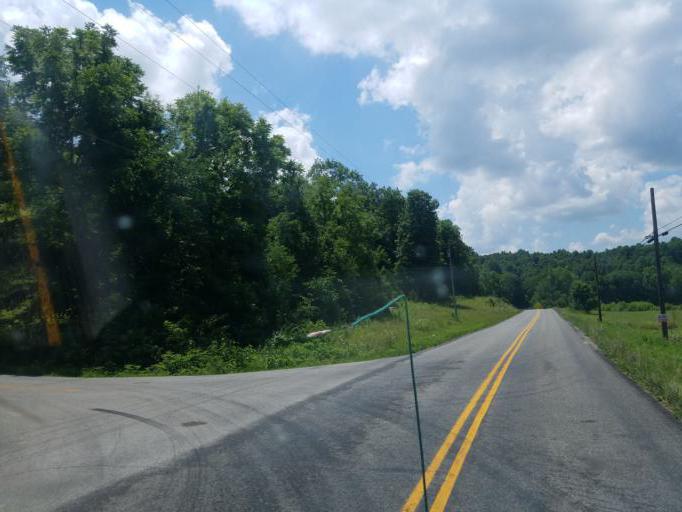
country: US
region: Kentucky
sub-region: Grayson County
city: Leitchfield
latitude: 37.5063
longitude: -86.4716
